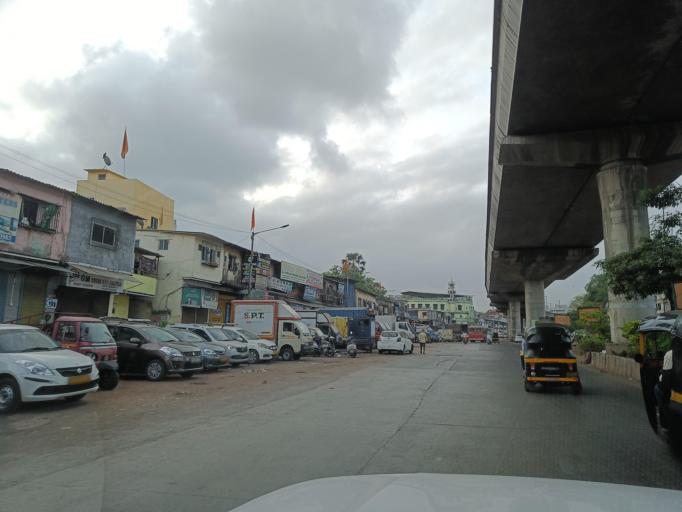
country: IN
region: Maharashtra
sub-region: Mumbai Suburban
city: Powai
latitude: 19.1024
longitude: 72.8896
